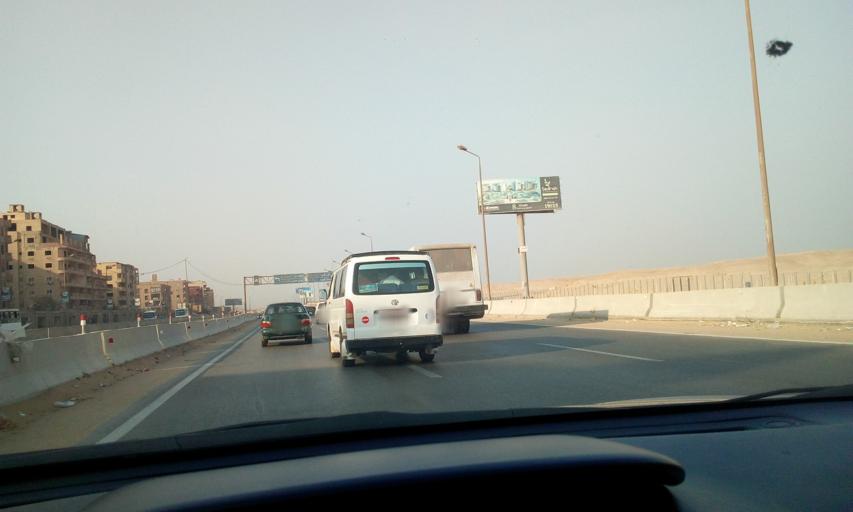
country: EG
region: Al Jizah
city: Al Jizah
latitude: 29.9613
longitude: 31.1085
